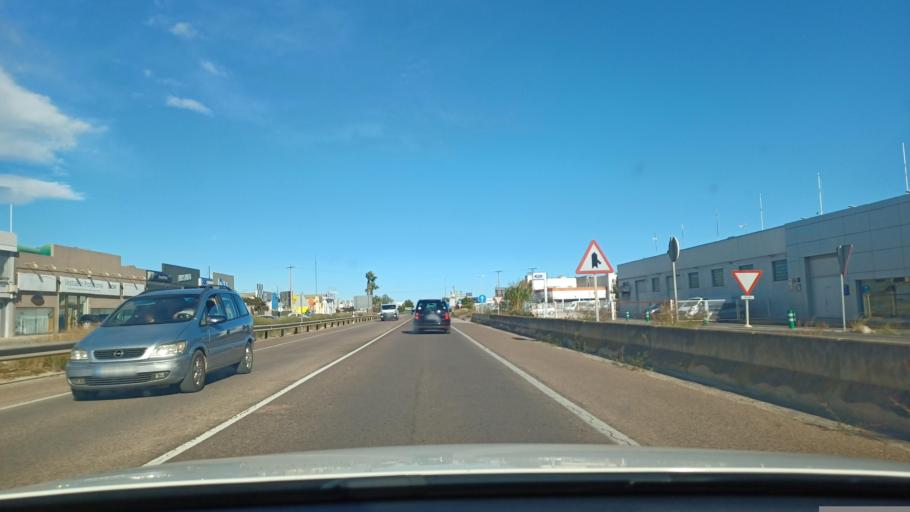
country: ES
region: Valencia
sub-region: Provincia de Castello
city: Vinaros
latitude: 40.4784
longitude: 0.4703
